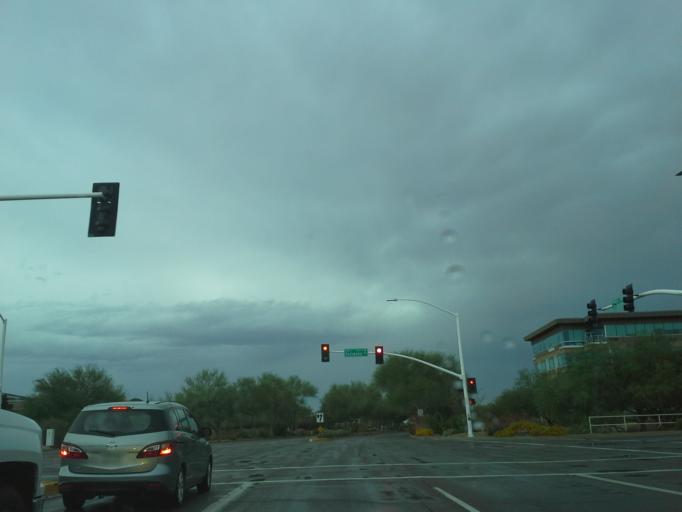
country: US
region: Arizona
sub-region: Maricopa County
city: Paradise Valley
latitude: 33.6449
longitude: -111.8974
